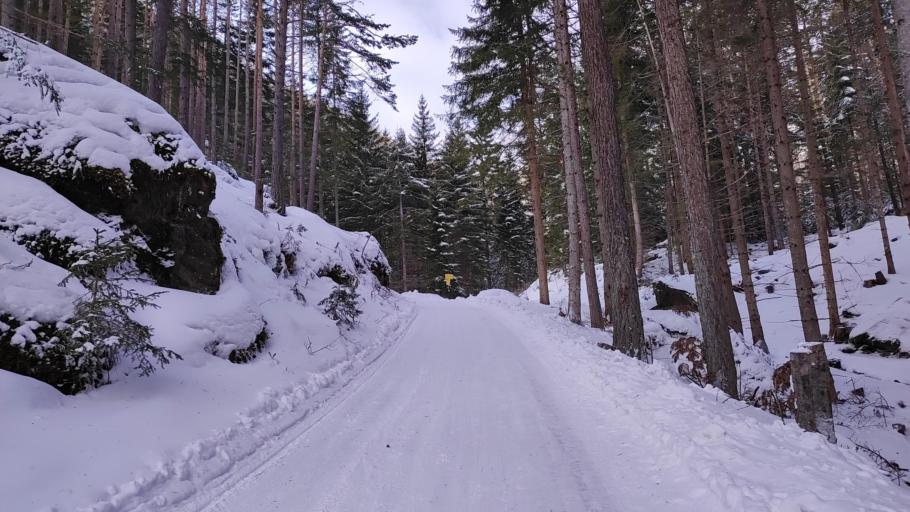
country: AT
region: Tyrol
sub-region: Politischer Bezirk Imst
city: Umhausen
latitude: 47.1013
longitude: 10.9345
